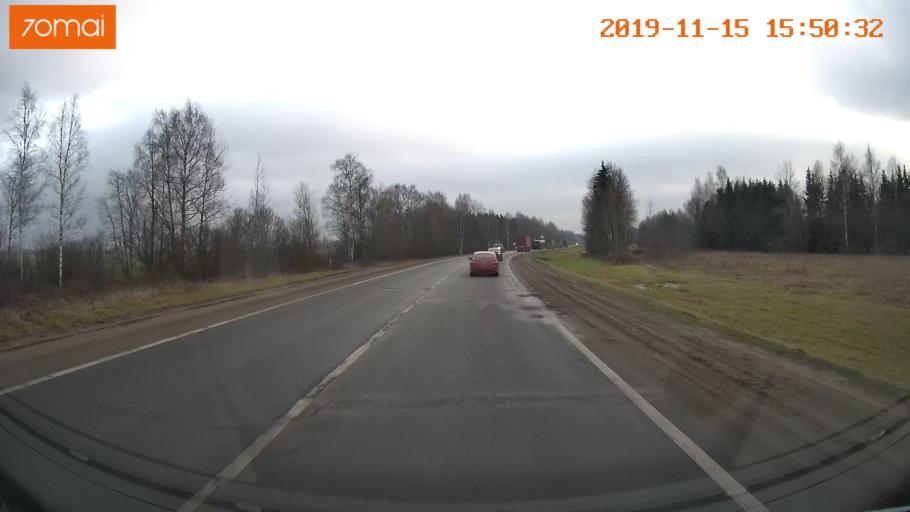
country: RU
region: Jaroslavl
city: Yaroslavl
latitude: 57.9046
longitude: 40.0134
